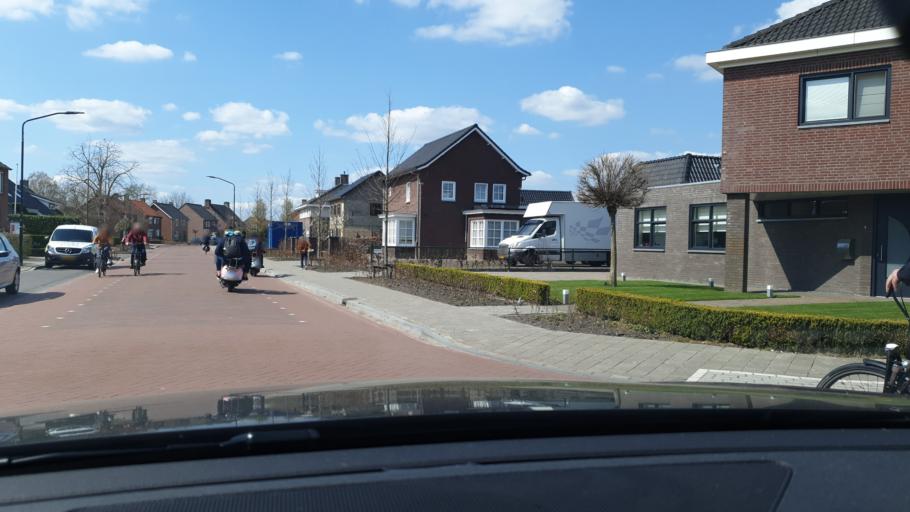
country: NL
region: North Brabant
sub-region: Gemeente Bladel en Netersel
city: Bladel
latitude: 51.3652
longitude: 5.2576
